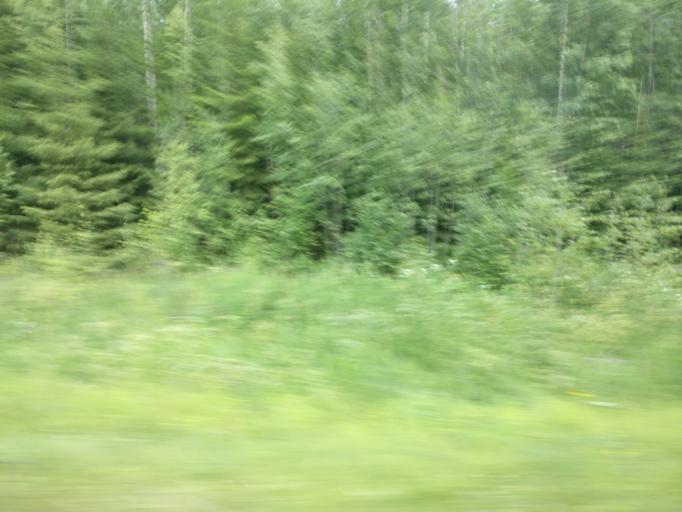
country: FI
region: Southern Savonia
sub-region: Pieksaemaeki
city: Joroinen
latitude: 62.2062
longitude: 27.9508
